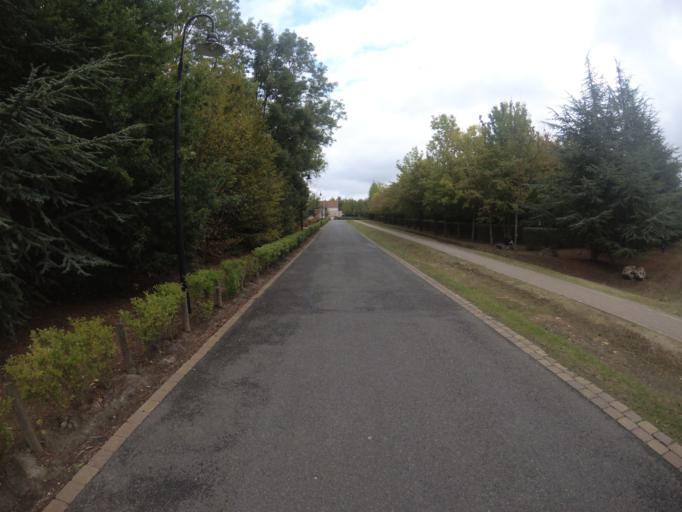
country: FR
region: Ile-de-France
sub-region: Departement de Seine-et-Marne
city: Chessy
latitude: 48.8760
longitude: 2.7610
